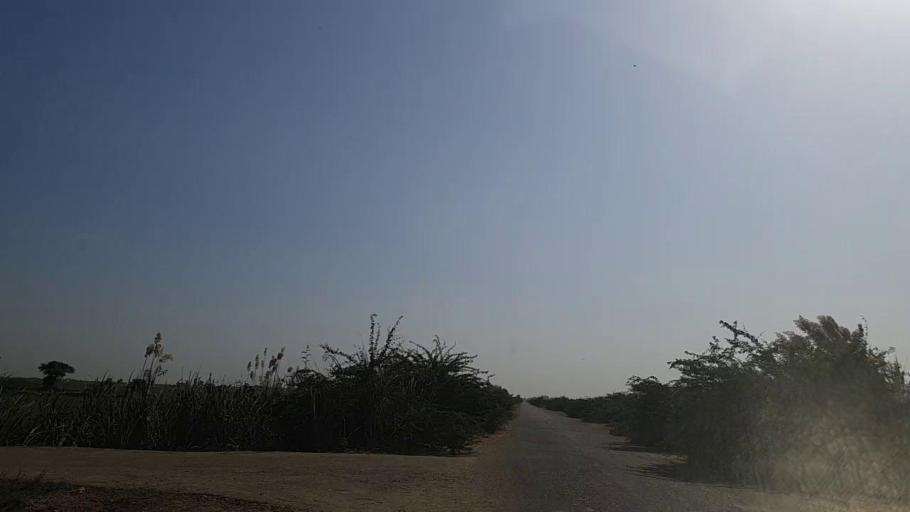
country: PK
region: Sindh
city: Jati
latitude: 24.4439
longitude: 68.2620
